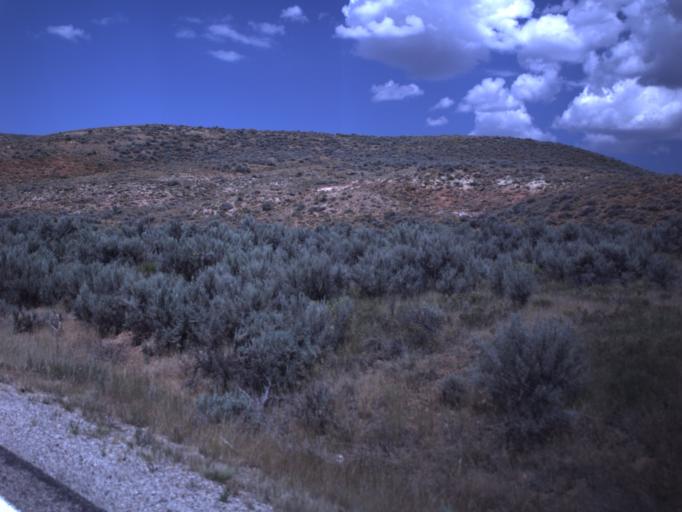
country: US
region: Utah
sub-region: Rich County
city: Randolph
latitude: 41.7751
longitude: -111.1791
